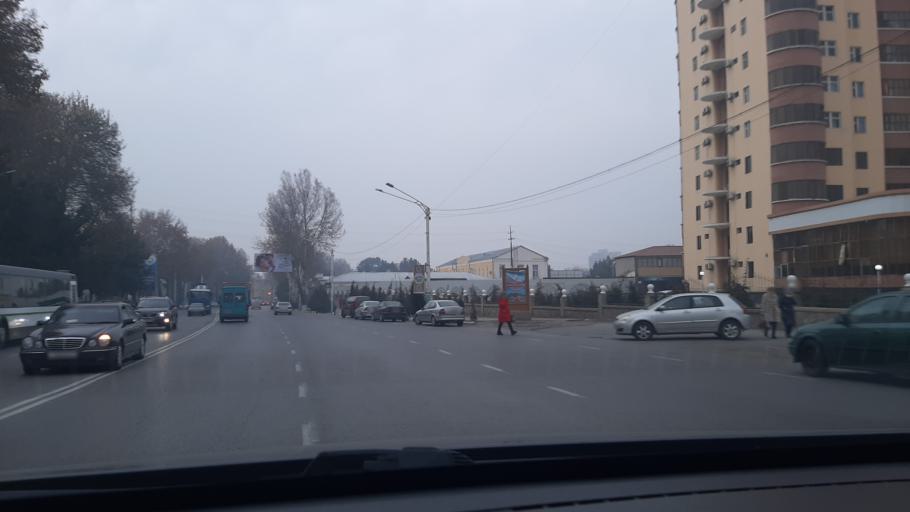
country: TJ
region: Viloyati Sughd
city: Khujand
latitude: 40.2723
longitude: 69.6422
